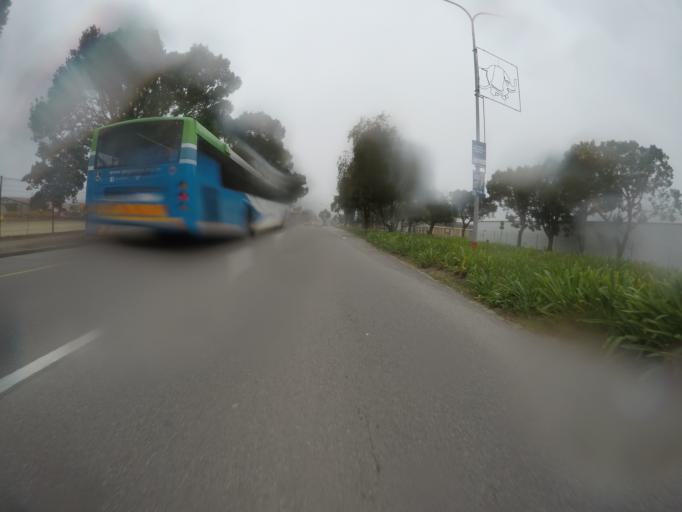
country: ZA
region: Western Cape
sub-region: Eden District Municipality
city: George
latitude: -33.9739
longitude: 22.4448
